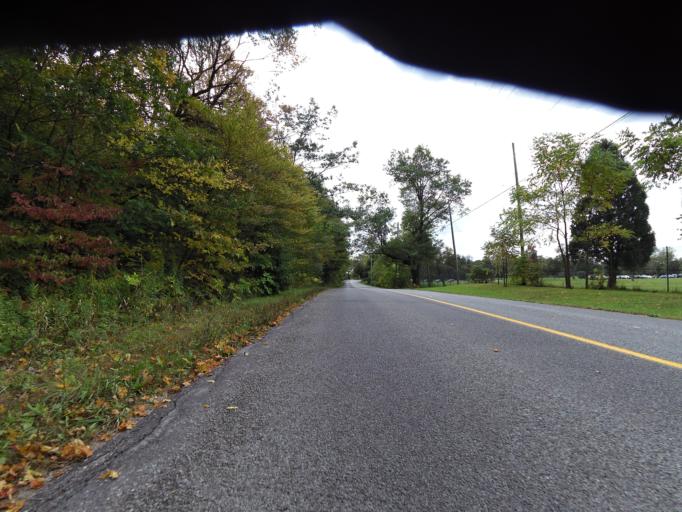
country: CA
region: Ontario
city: Burlington
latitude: 43.3709
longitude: -79.8809
